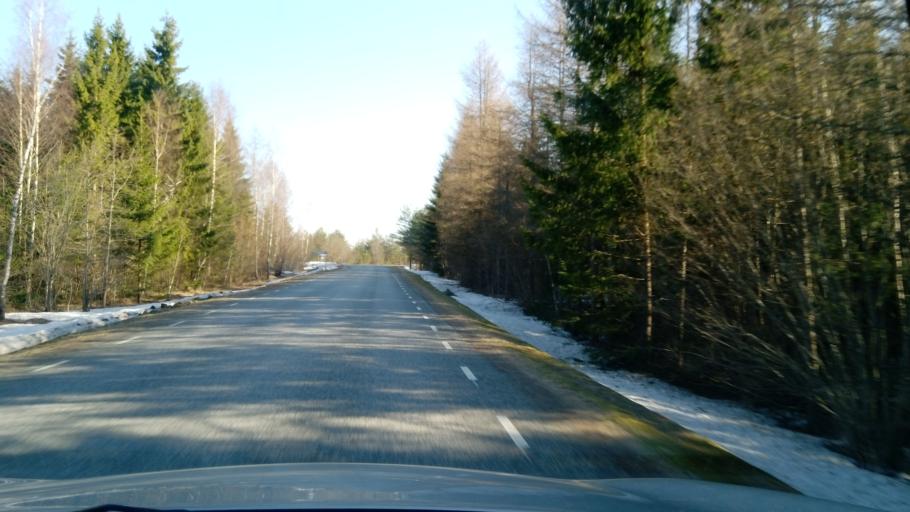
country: EE
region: Laeaene-Virumaa
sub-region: Kadrina vald
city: Kadrina
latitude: 59.2390
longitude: 26.1757
